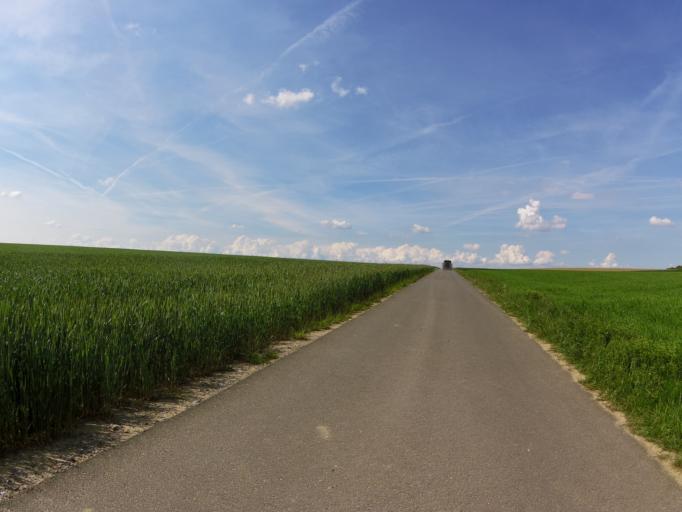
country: DE
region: Bavaria
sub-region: Regierungsbezirk Unterfranken
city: Theilheim
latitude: 49.7369
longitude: 10.0248
